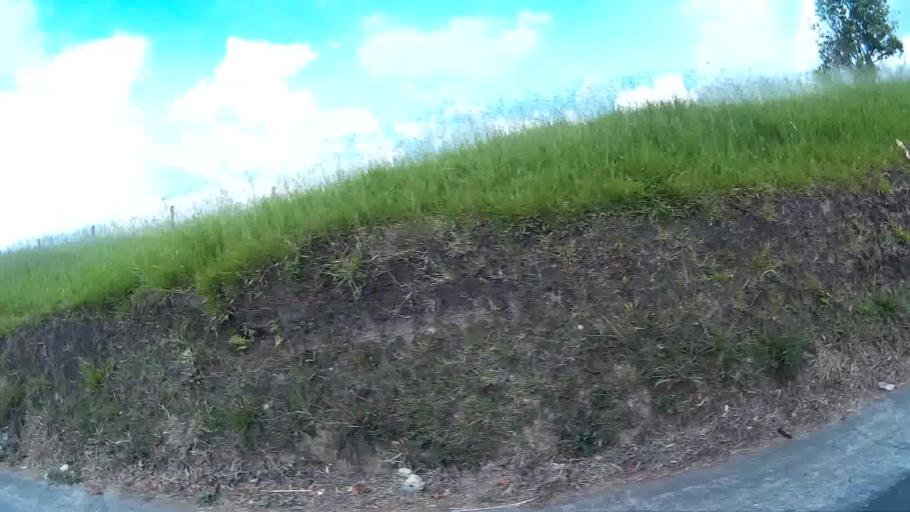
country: CO
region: Quindio
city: Circasia
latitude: 4.6034
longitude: -75.6353
